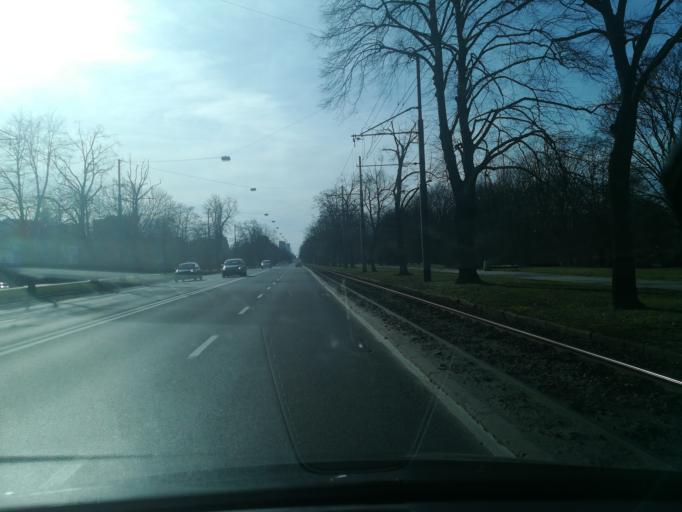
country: PL
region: Masovian Voivodeship
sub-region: Warszawa
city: Praga Poludnie
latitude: 52.2417
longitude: 21.0687
